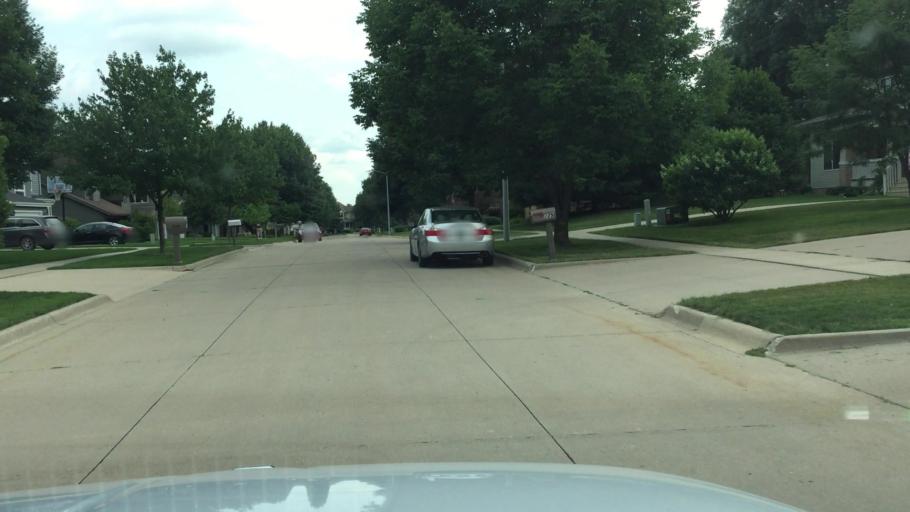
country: US
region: Iowa
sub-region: Johnson County
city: Iowa City
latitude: 41.6656
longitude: -91.4938
